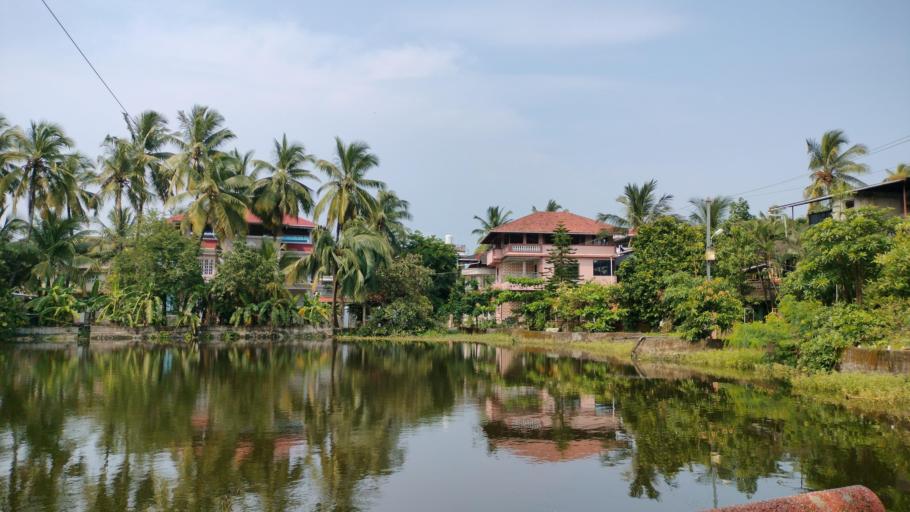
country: IN
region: Maharashtra
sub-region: Thane
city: Virar
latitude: 19.4135
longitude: 72.7874
